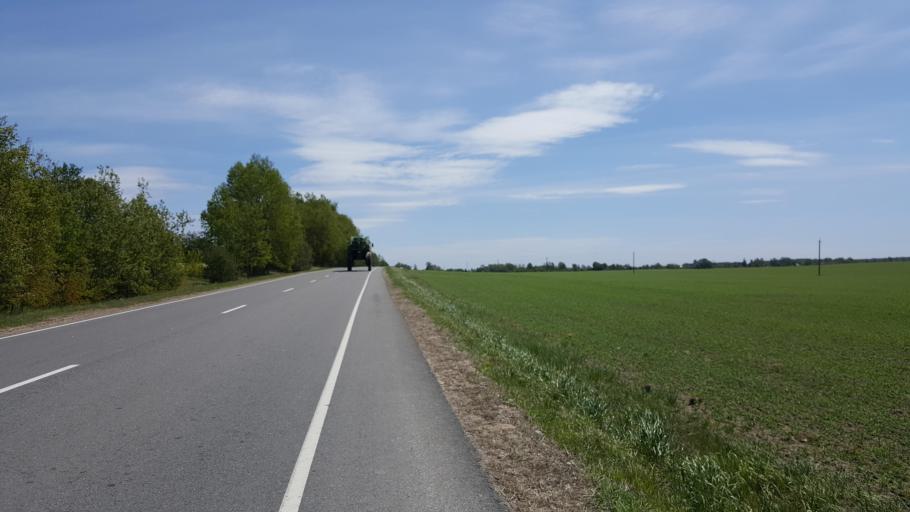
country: BY
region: Brest
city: Zhabinka
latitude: 52.3575
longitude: 24.1689
